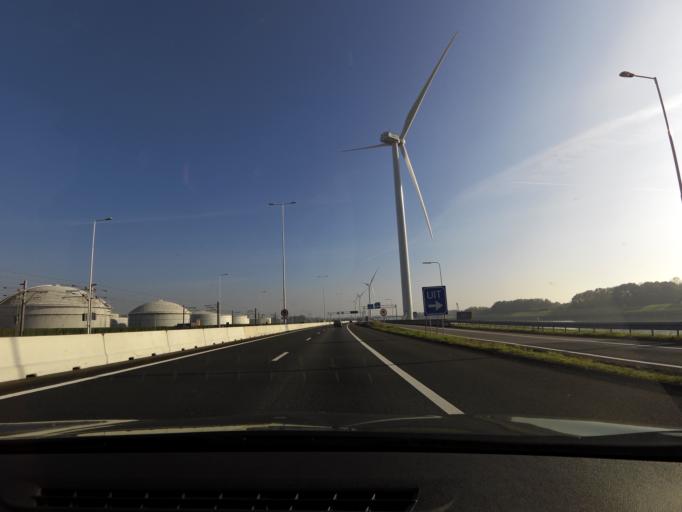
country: NL
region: South Holland
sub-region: Gemeente Brielle
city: Brielle
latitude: 51.9083
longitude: 4.2016
